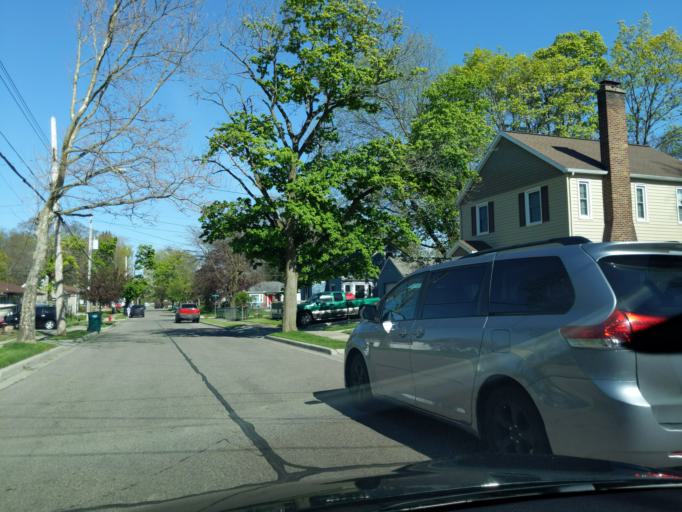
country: US
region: Michigan
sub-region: Ingham County
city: Lansing
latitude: 42.7096
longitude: -84.5662
